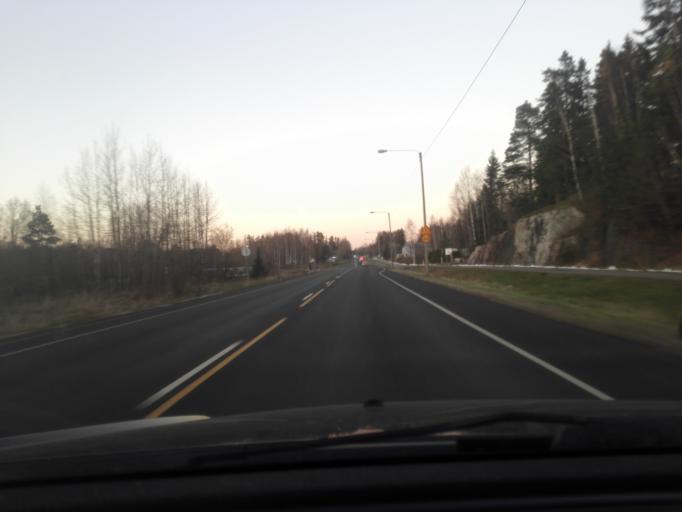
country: FI
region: Uusimaa
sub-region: Helsinki
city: Kerava
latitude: 60.3388
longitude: 25.1251
